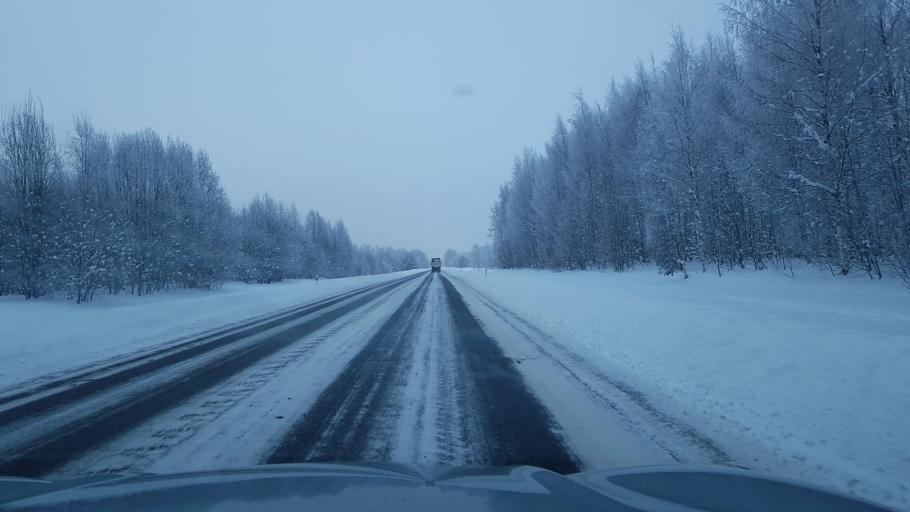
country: EE
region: Ida-Virumaa
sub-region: Johvi vald
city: Johvi
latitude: 59.2153
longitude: 27.3395
